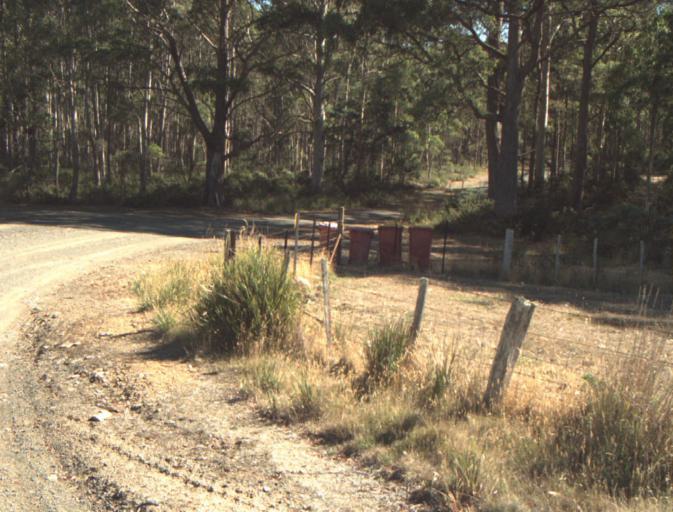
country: AU
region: Tasmania
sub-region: Launceston
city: Newstead
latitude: -41.3051
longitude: 147.3169
